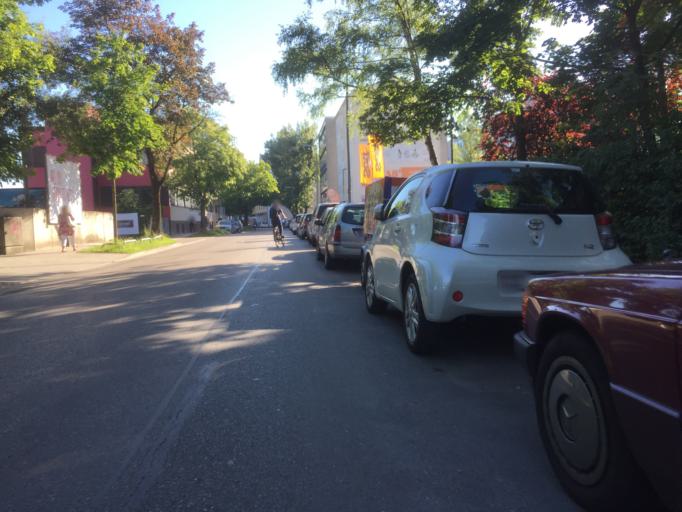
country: DE
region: Bavaria
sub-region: Upper Bavaria
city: Bogenhausen
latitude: 48.1277
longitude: 11.6079
